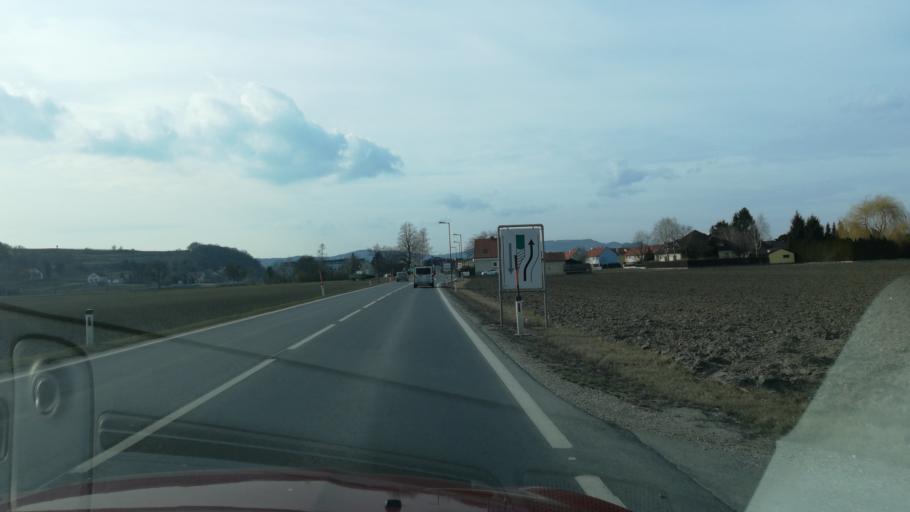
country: AT
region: Lower Austria
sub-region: Politischer Bezirk Sankt Polten
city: Traismauer
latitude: 48.3482
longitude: 15.7611
